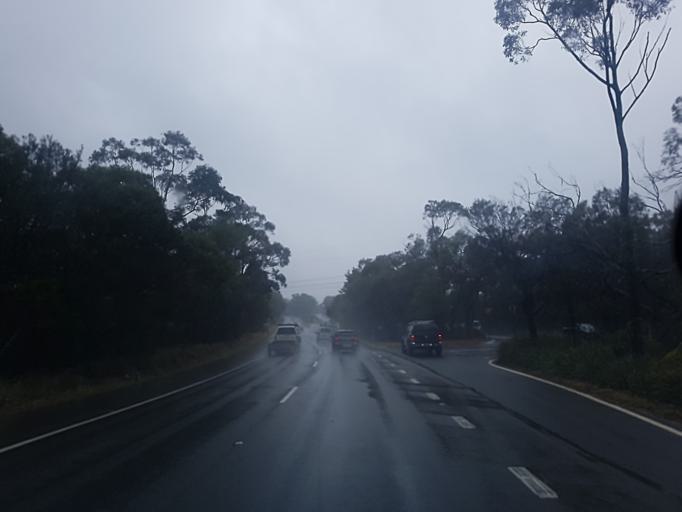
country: AU
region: New South Wales
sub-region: Warringah
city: Davidson
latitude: -33.7075
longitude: 151.2024
